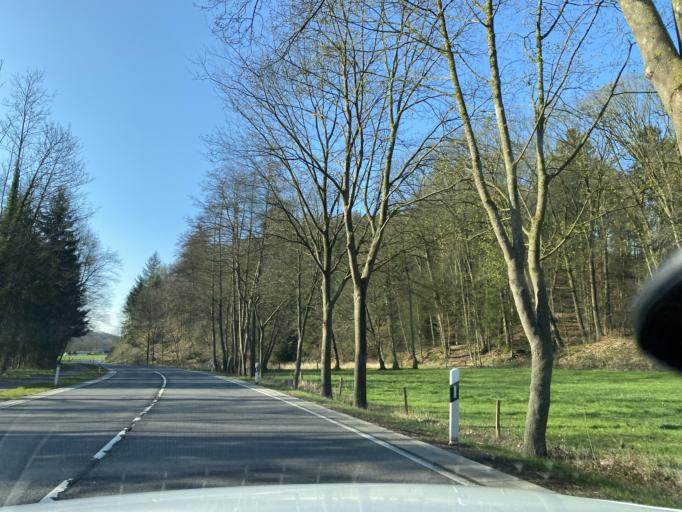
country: DE
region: North Rhine-Westphalia
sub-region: Regierungsbezirk Koln
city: Odenthal
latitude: 51.0457
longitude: 7.1238
